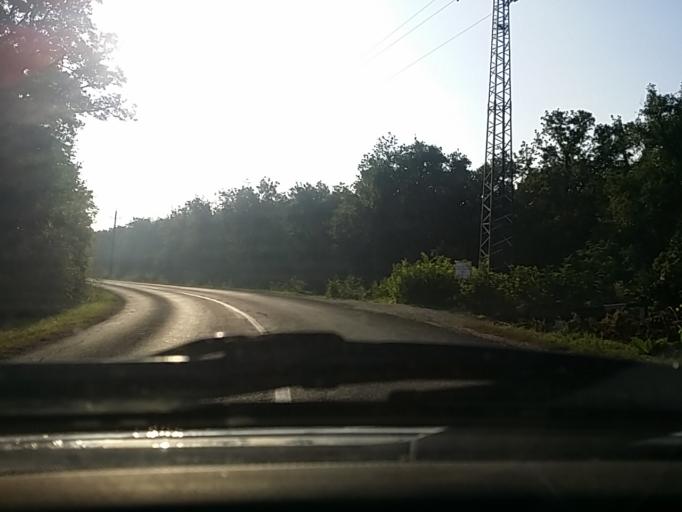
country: HU
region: Pest
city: Nagykovacsi
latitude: 47.7033
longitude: 19.0216
